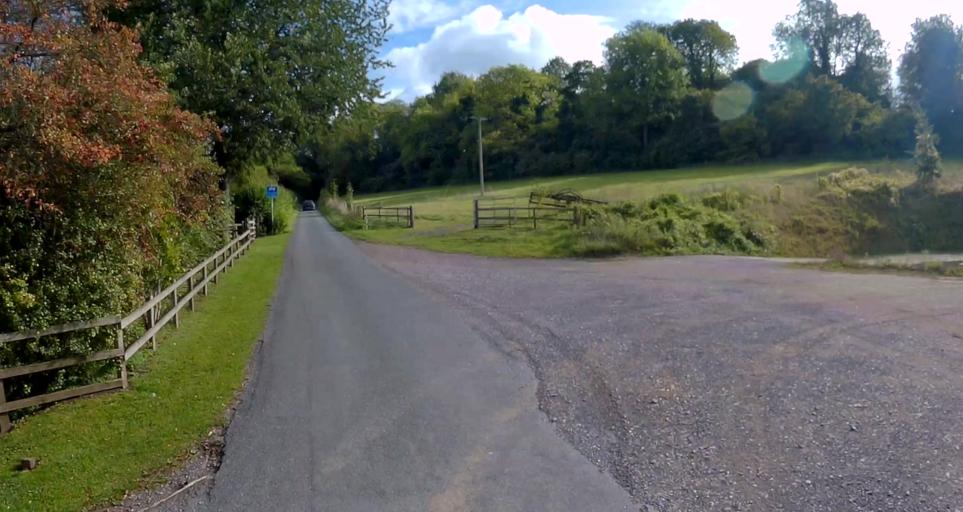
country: GB
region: England
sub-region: Hampshire
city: Kings Worthy
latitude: 51.0861
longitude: -1.2166
